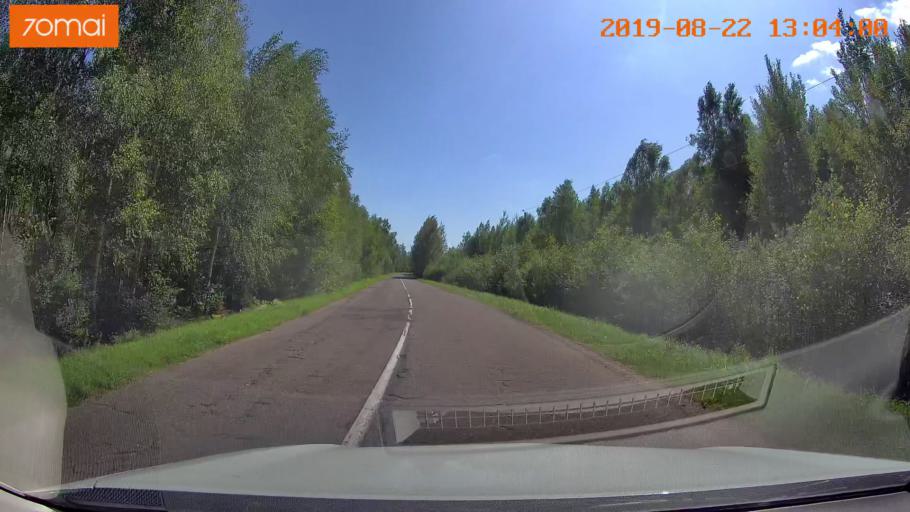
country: BY
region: Minsk
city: Prawdzinski
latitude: 53.3750
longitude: 27.8219
